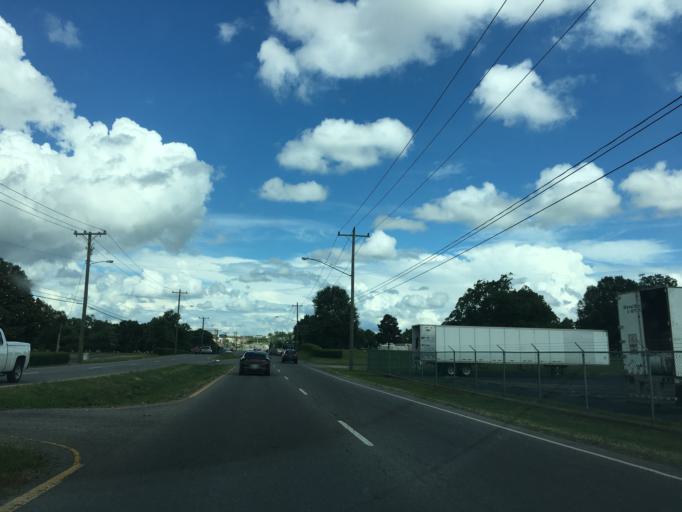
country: US
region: Tennessee
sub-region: Davidson County
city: Oak Hill
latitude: 36.1119
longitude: -86.7624
